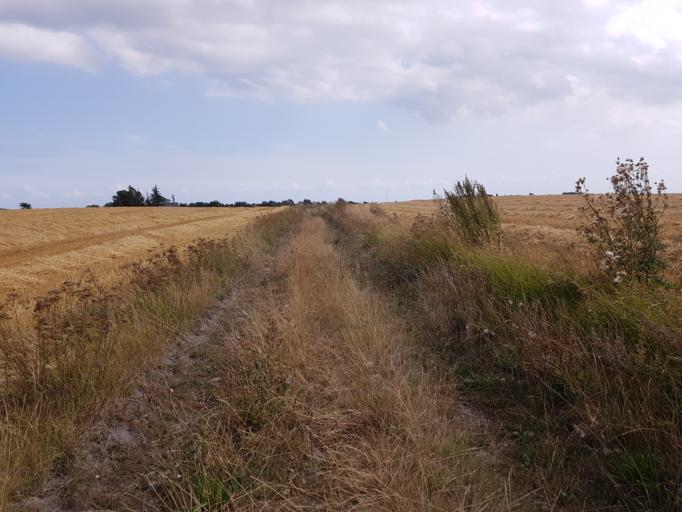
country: DK
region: Zealand
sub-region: Guldborgsund Kommune
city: Nykobing Falster
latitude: 54.5969
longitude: 11.9239
